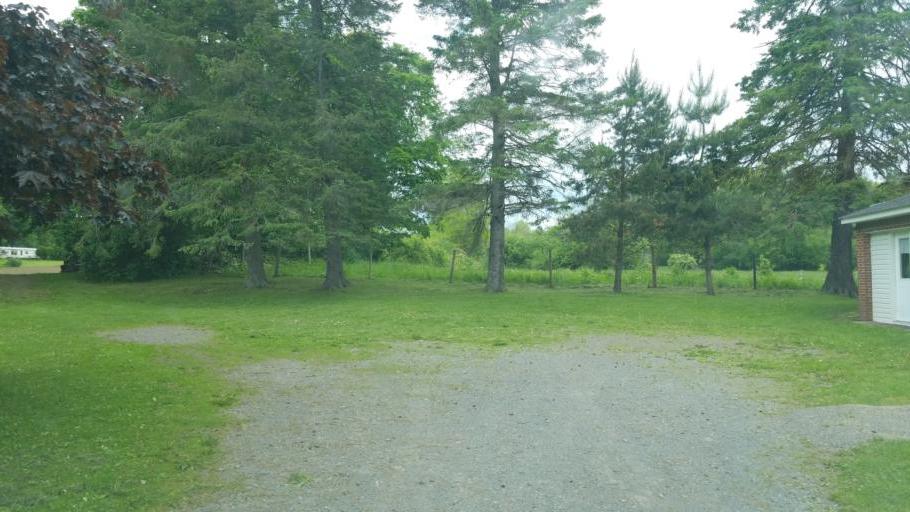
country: US
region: New York
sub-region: Herkimer County
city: Frankfort
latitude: 42.9077
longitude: -75.1525
